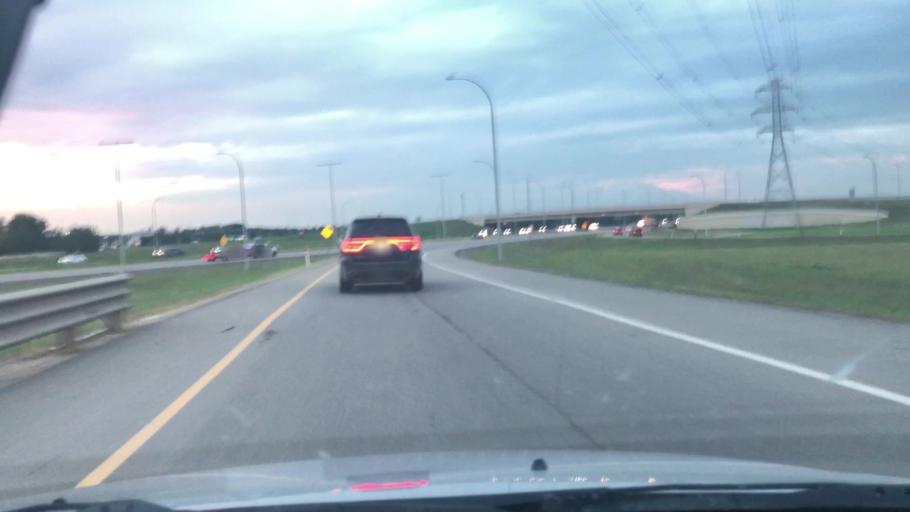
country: CA
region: Alberta
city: St. Albert
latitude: 53.5197
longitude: -113.6578
